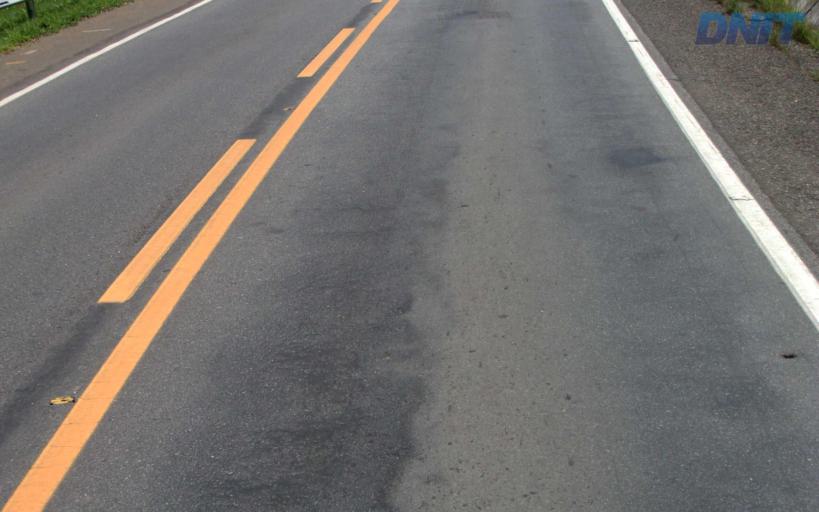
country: BR
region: Minas Gerais
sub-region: Governador Valadares
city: Governador Valadares
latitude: -19.0241
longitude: -42.1462
